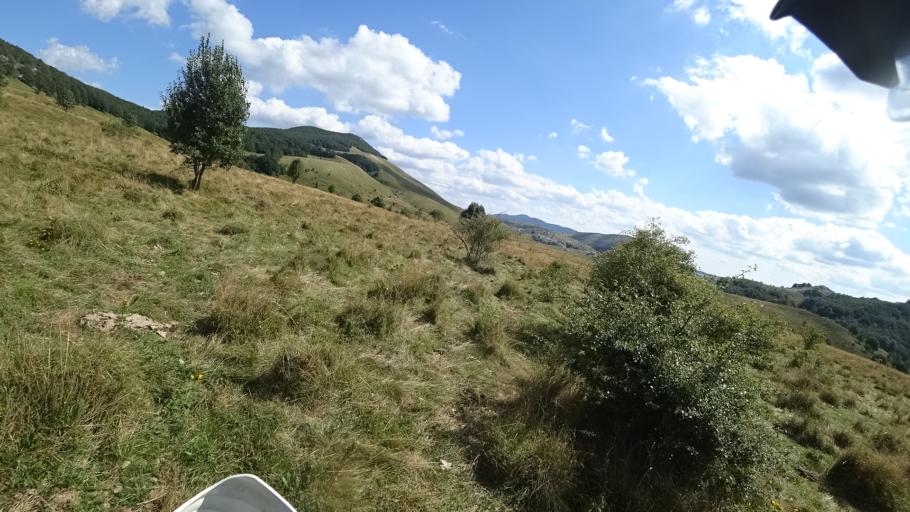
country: HR
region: Zadarska
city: Gracac
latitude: 44.4190
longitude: 15.9991
